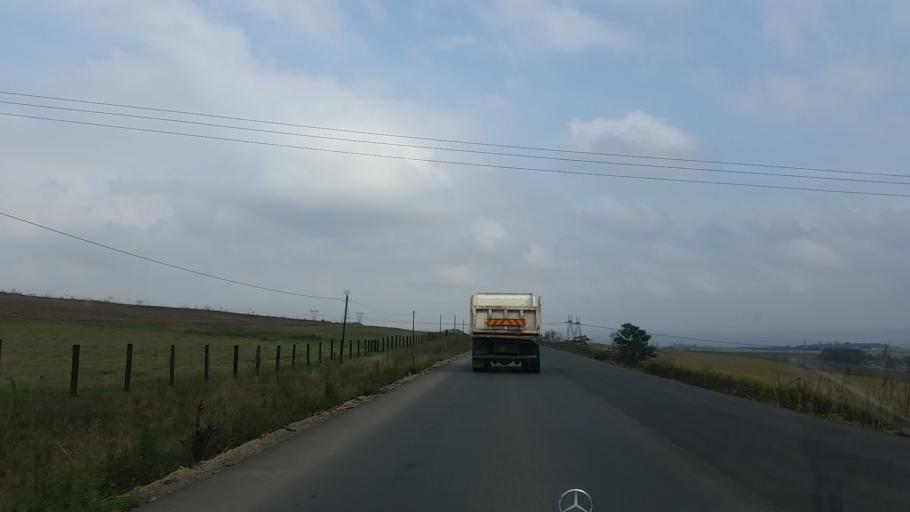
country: ZA
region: KwaZulu-Natal
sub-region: uMgungundlovu District Municipality
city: Camperdown
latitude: -29.7617
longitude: 30.5075
